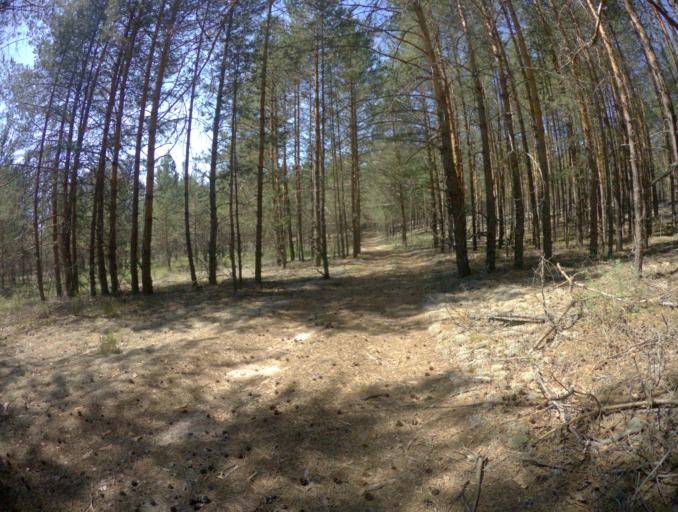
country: RU
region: Ivanovo
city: Talitsy
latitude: 56.3784
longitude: 42.3073
